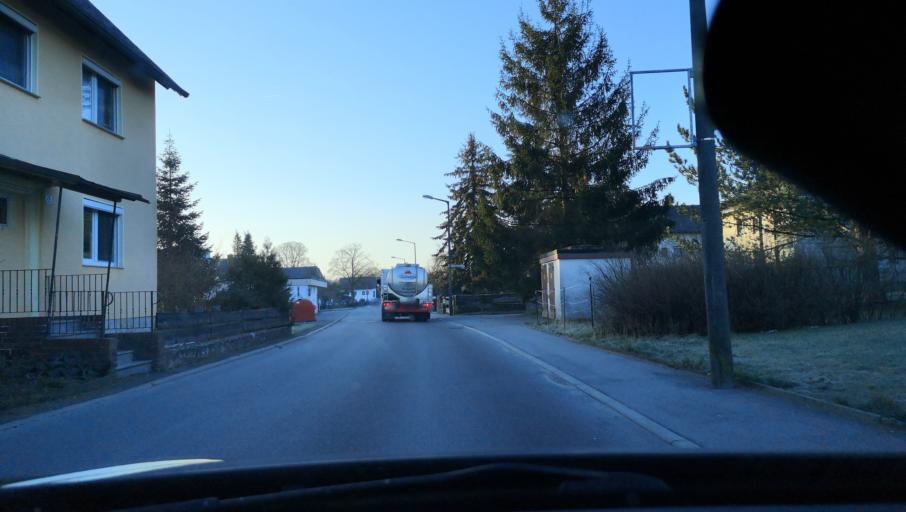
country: DE
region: Bavaria
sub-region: Upper Franconia
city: Neustadt bei Coburg
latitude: 50.3165
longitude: 11.1019
